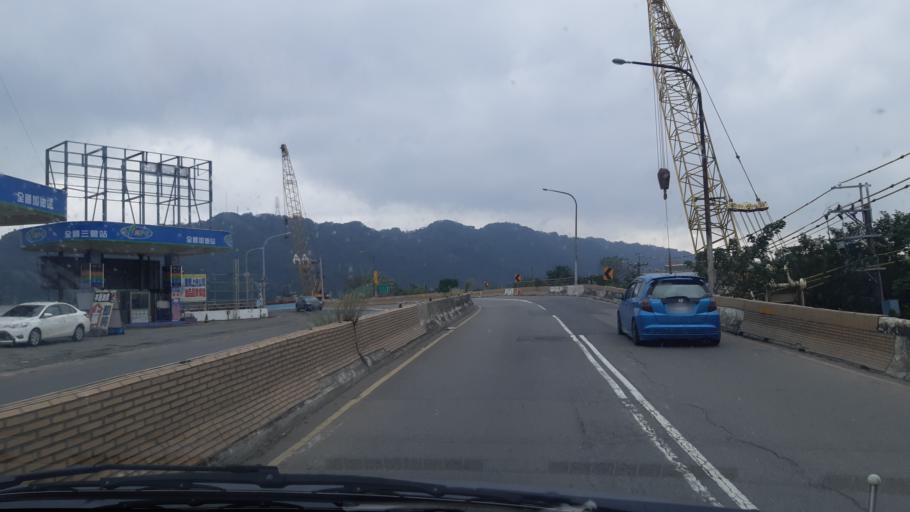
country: TW
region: Taiwan
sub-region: Taoyuan
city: Taoyuan
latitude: 24.9468
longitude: 121.3526
